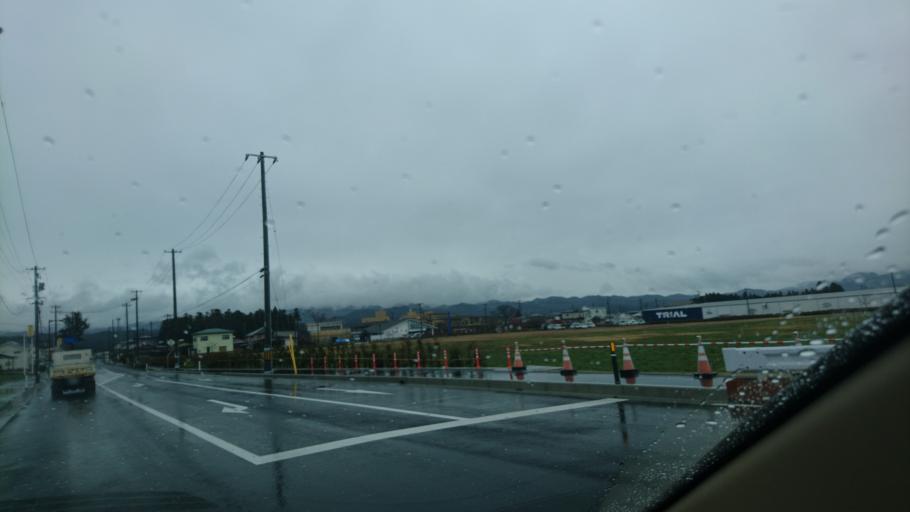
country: JP
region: Iwate
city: Mizusawa
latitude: 39.1183
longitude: 141.1611
